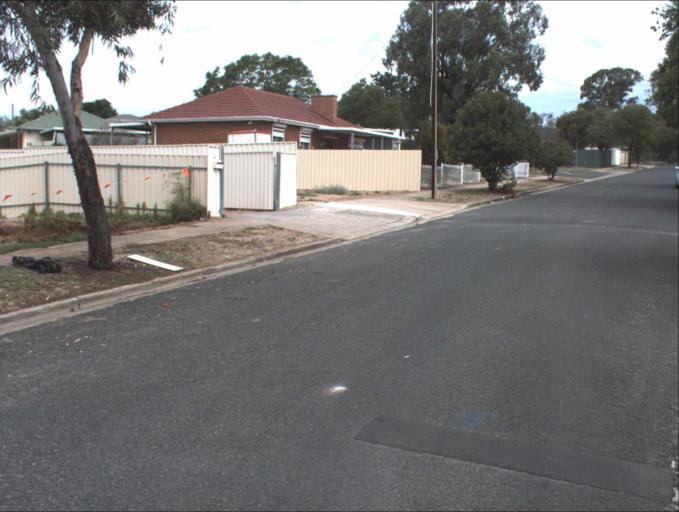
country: AU
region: South Australia
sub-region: Port Adelaide Enfield
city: Enfield
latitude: -34.8571
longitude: 138.6049
